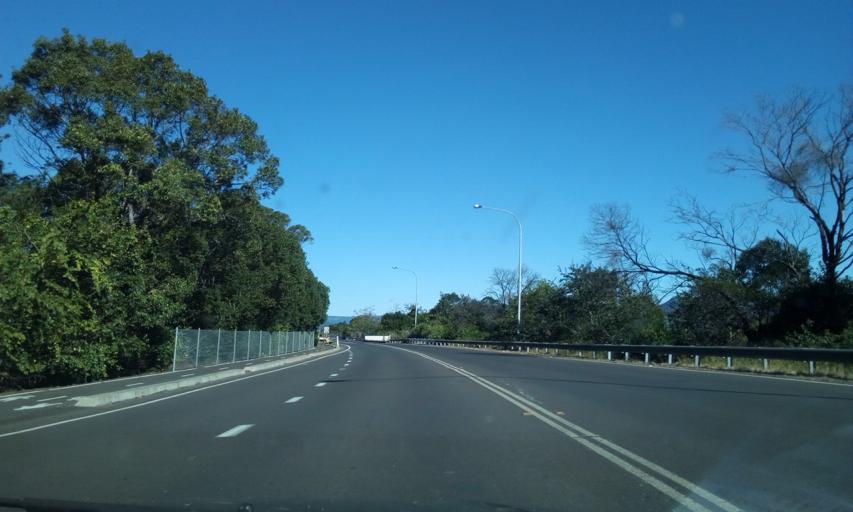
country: AU
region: New South Wales
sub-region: Wollongong
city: Koonawarra
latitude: -34.4753
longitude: 150.8101
